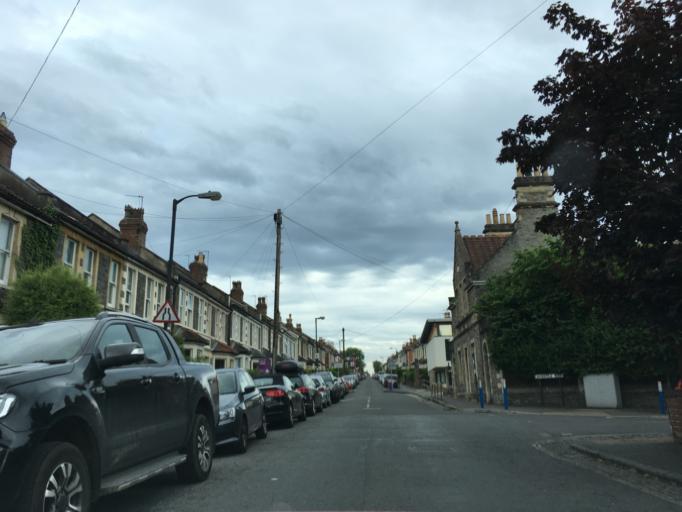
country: GB
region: England
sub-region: Bristol
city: Bristol
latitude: 51.4795
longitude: -2.5932
